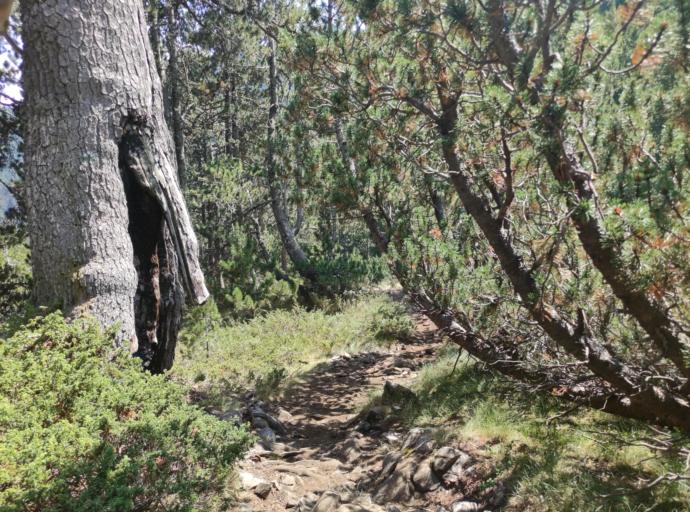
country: BG
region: Blagoevgrad
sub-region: Obshtina Bansko
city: Bansko
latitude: 41.7725
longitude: 23.4232
